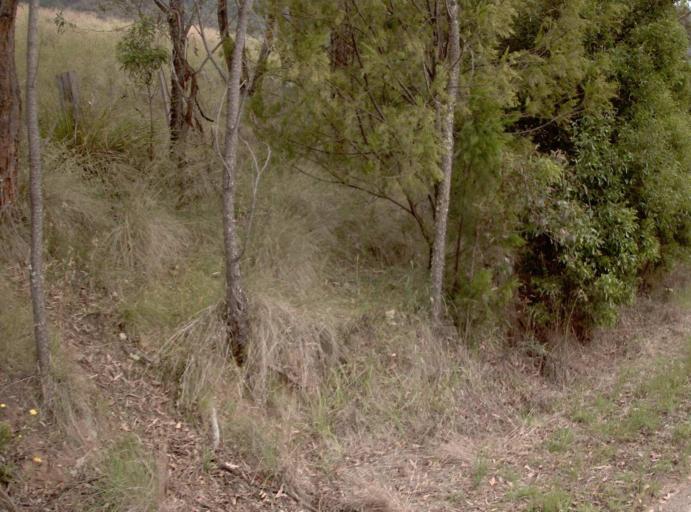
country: AU
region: Victoria
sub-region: East Gippsland
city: Bairnsdale
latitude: -37.5717
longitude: 147.1870
